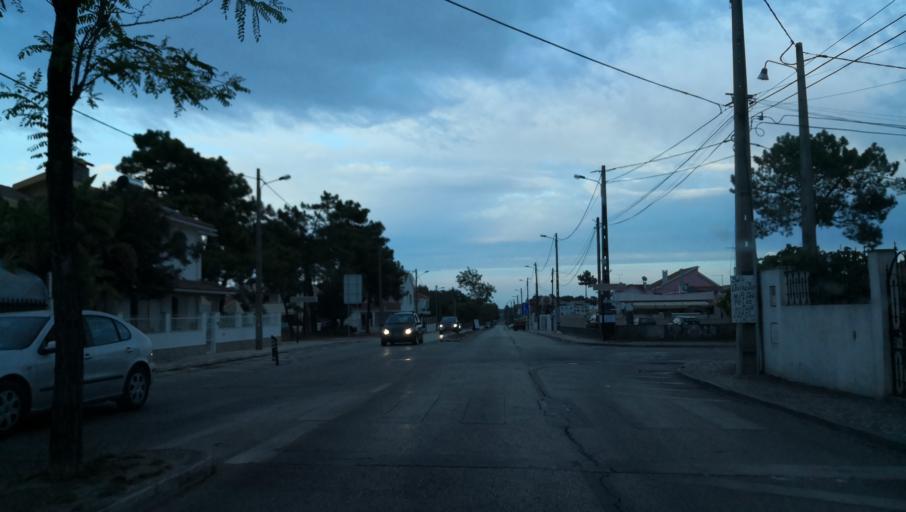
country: PT
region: Setubal
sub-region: Almada
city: Charneca
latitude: 38.6005
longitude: -9.1850
